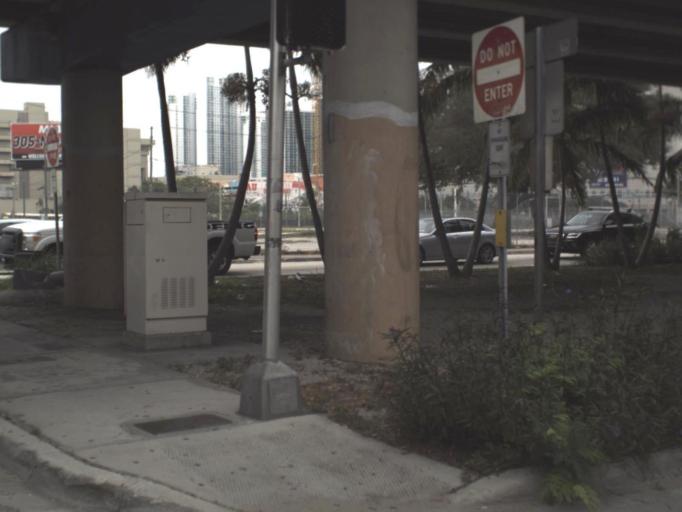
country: US
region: Florida
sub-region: Miami-Dade County
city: Miami
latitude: 25.7858
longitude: -80.1923
